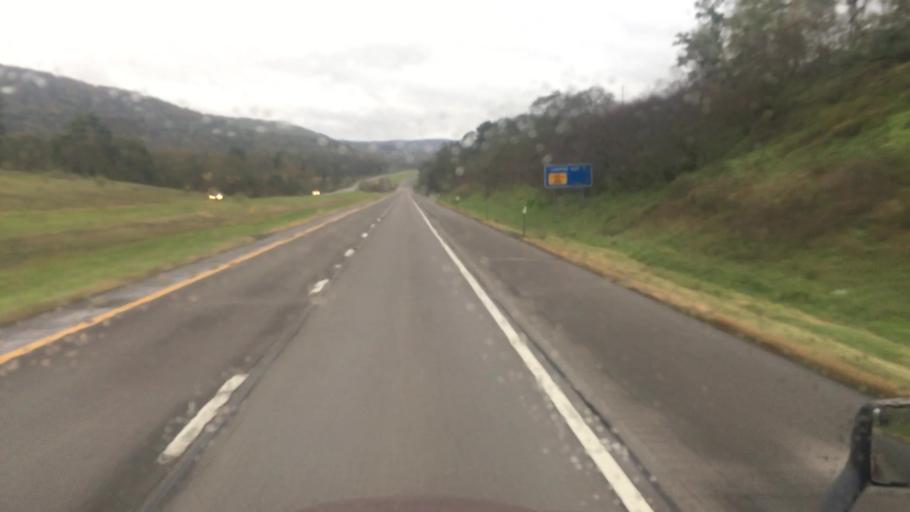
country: US
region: New York
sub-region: Otsego County
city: Unadilla
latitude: 42.3466
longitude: -75.2663
